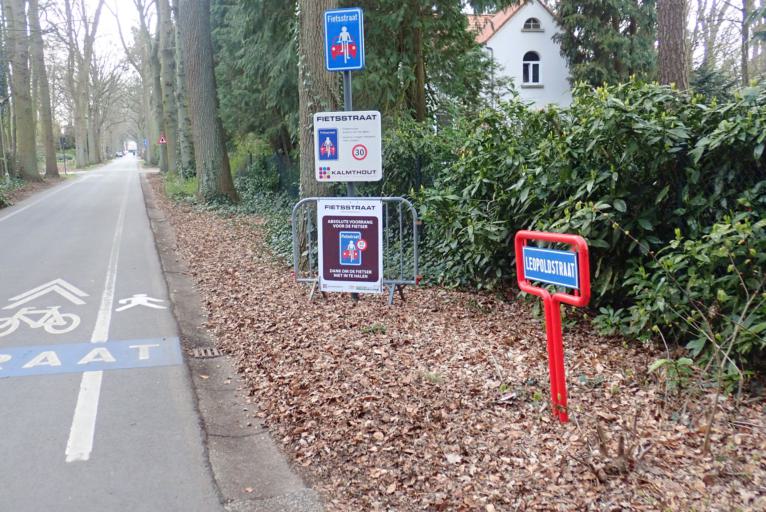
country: BE
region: Flanders
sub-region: Provincie Antwerpen
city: Kalmthout
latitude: 51.3713
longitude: 4.4673
